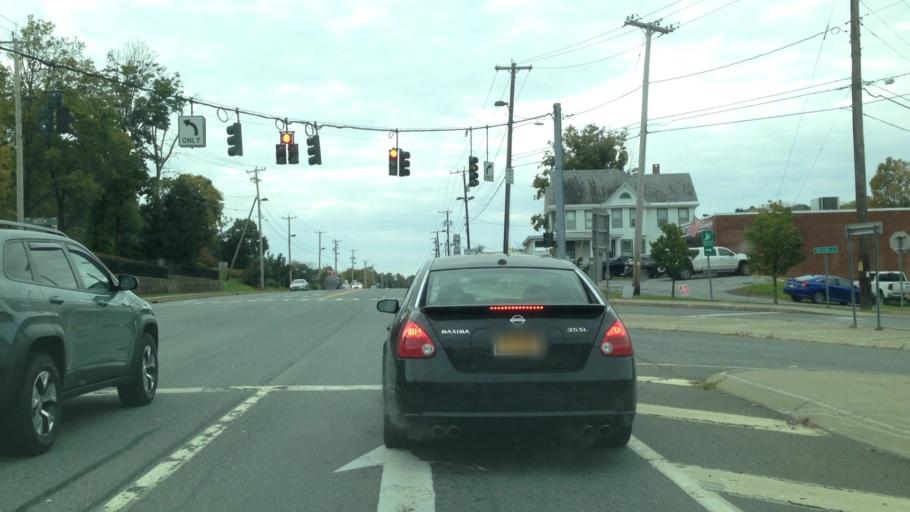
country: US
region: New York
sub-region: Ulster County
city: Highland
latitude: 41.7169
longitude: -73.9629
